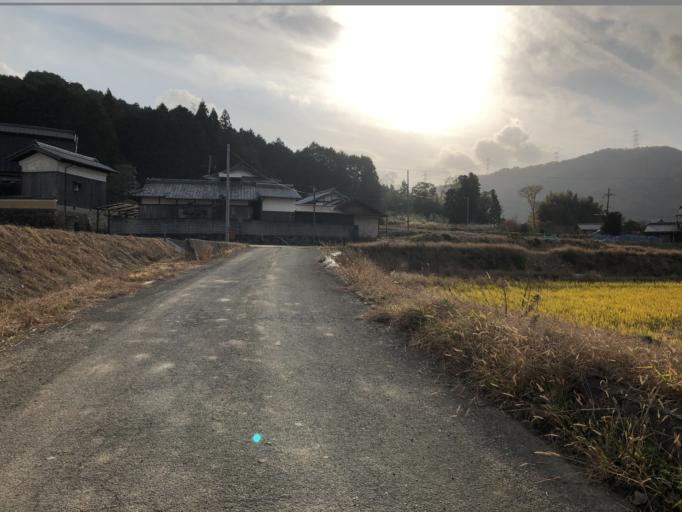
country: JP
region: Kyoto
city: Kameoka
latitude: 35.0056
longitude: 135.4854
